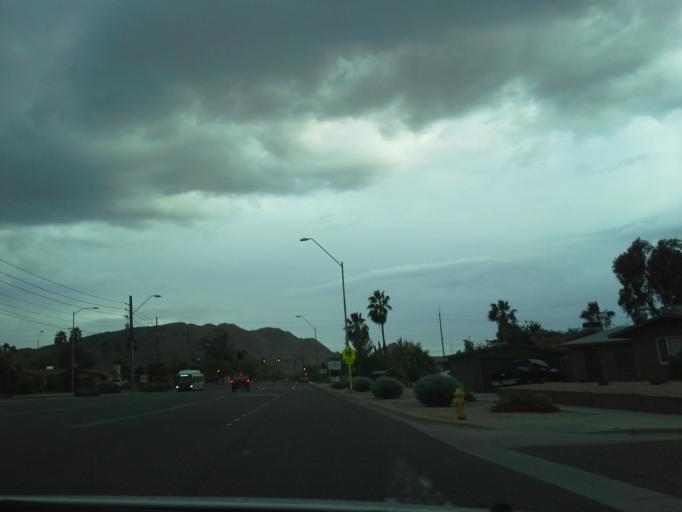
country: US
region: Arizona
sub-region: Maricopa County
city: Paradise Valley
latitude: 33.5843
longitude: -111.9958
